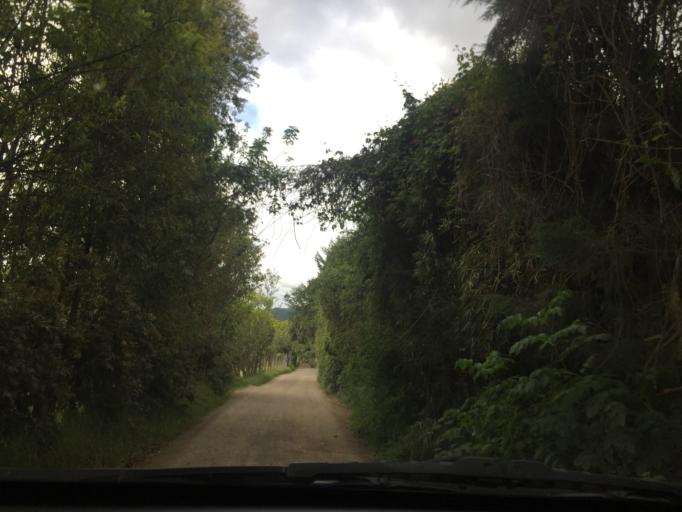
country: CO
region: Cundinamarca
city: Subachoque
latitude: 4.9373
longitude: -74.1483
